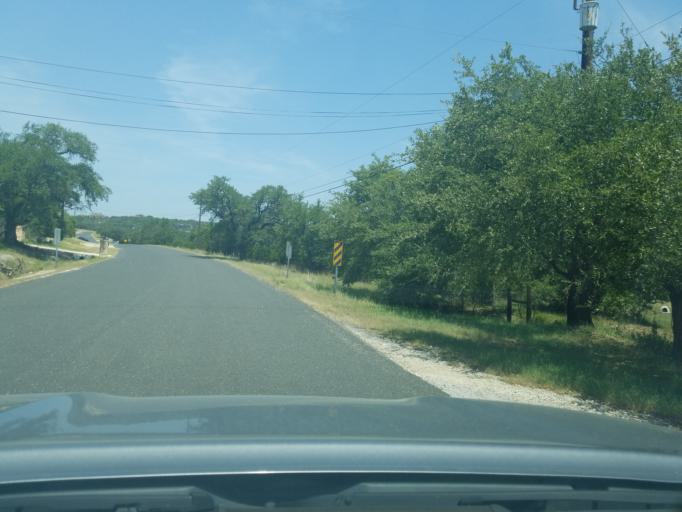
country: US
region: Texas
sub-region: Bexar County
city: Timberwood Park
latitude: 29.6731
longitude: -98.5076
